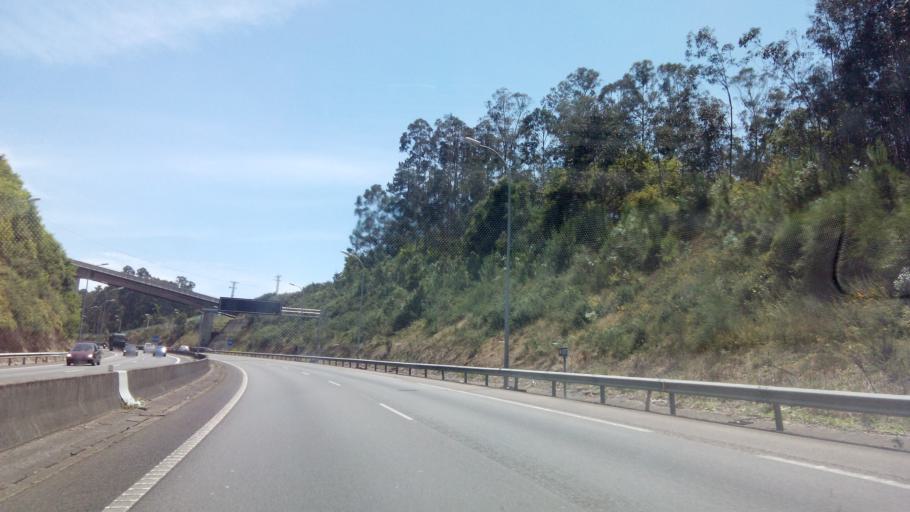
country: ES
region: Galicia
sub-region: Provincia de Pontevedra
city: Vigo
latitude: 42.2437
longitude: -8.6823
